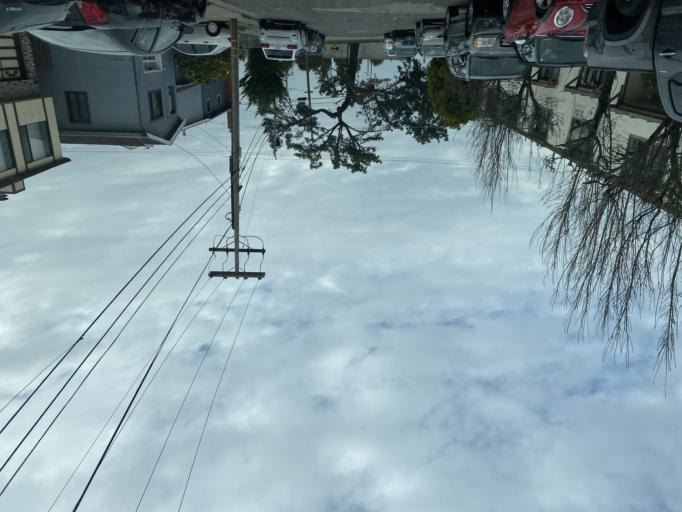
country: US
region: California
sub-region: San Mateo County
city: Millbrae
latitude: 37.6053
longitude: -122.3938
